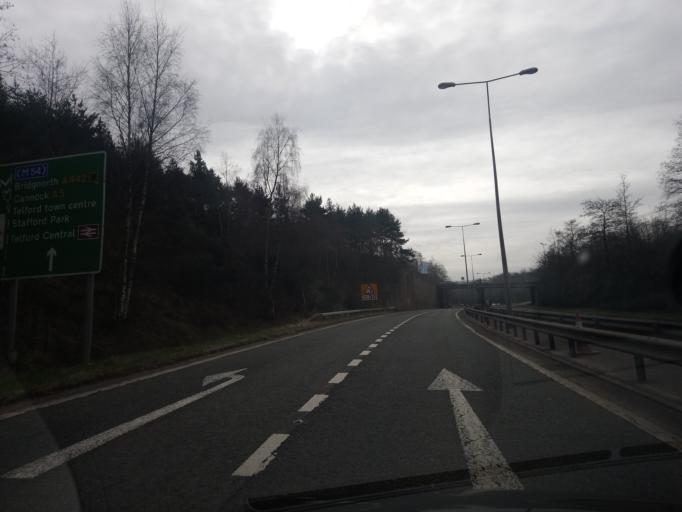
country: GB
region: England
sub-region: Telford and Wrekin
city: Oakengates
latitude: 52.6902
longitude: -2.4451
